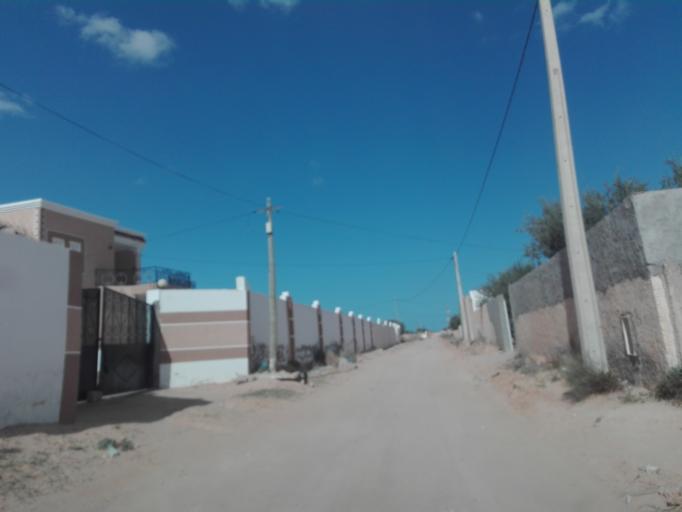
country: TN
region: Madanin
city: Bin Qirdan
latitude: 33.1611
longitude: 11.1952
